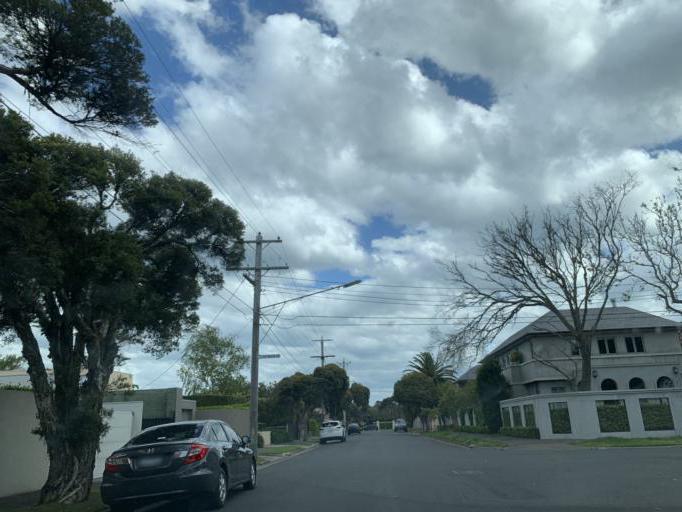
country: AU
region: Victoria
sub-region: Bayside
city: Hampton
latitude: -37.9274
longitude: 144.9987
